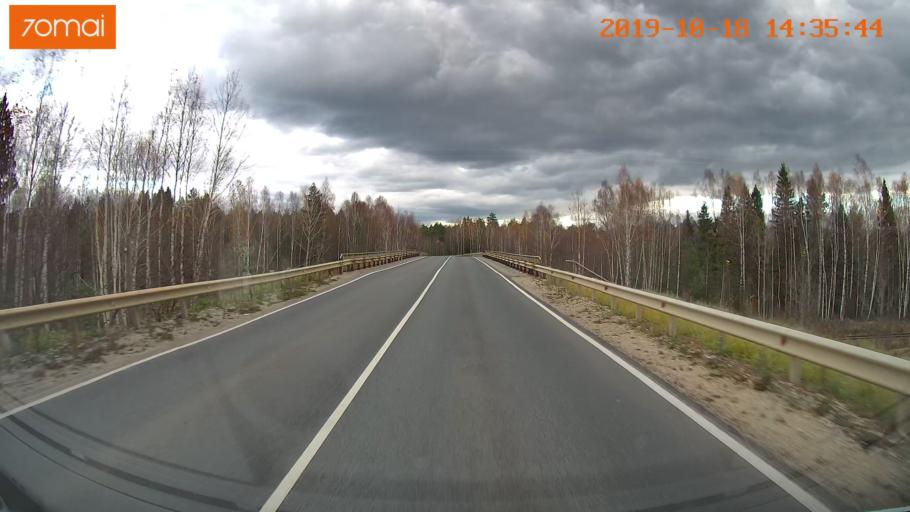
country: RU
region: Vladimir
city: Velikodvorskiy
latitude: 55.2219
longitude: 40.6449
